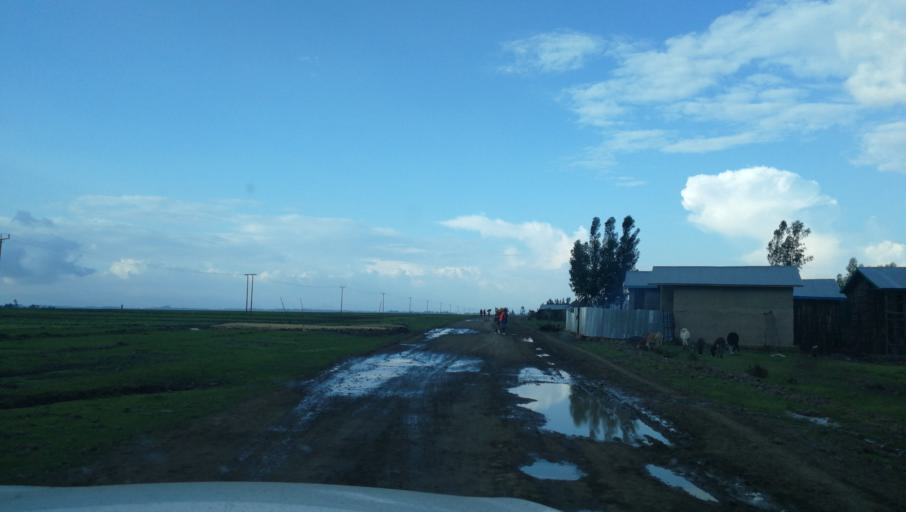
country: ET
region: Amhara
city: Were Ilu
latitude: 10.4416
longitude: 39.2562
